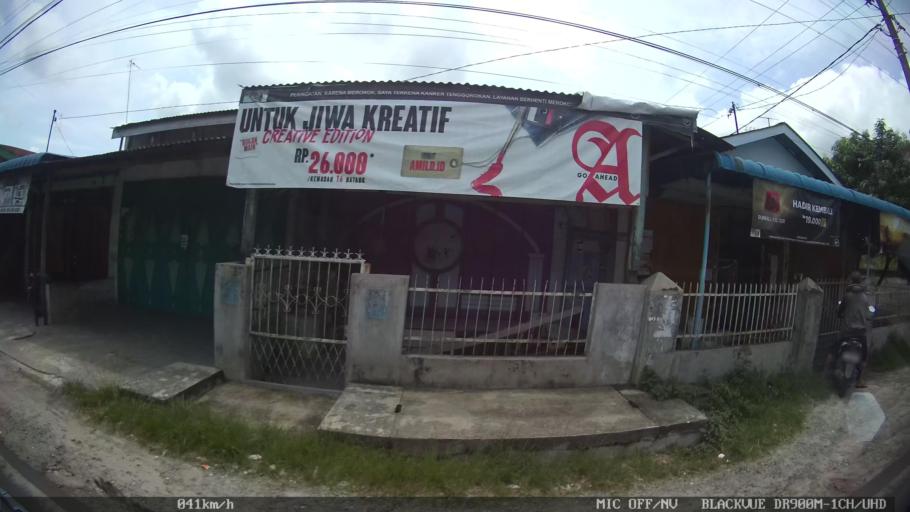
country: ID
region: North Sumatra
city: Percut
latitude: 3.5722
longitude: 98.8831
